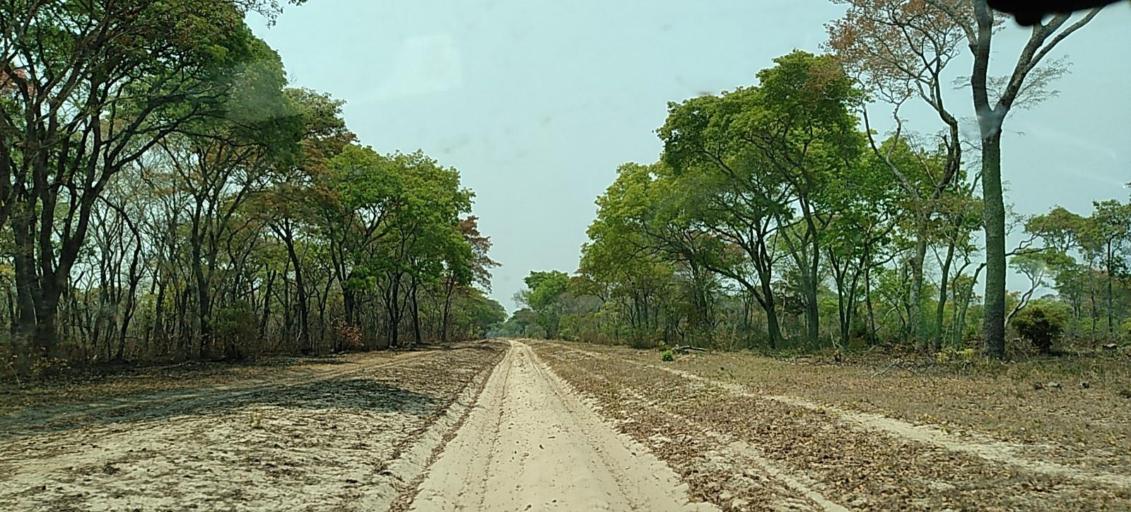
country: ZM
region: Western
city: Lukulu
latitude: -14.1393
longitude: 23.2801
